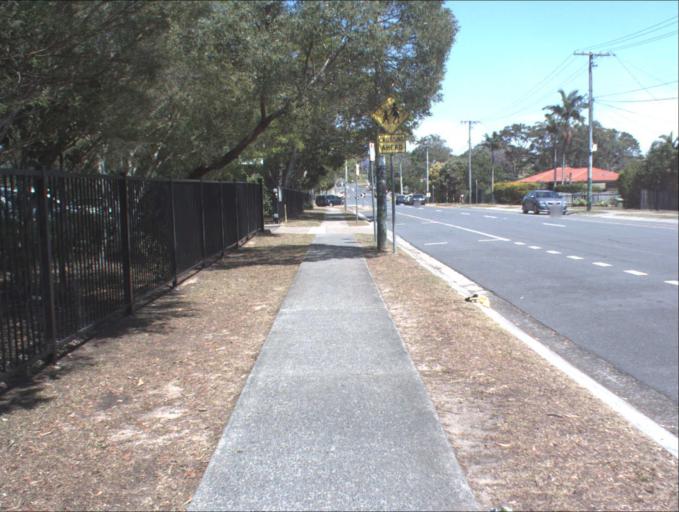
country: AU
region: Queensland
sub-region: Logan
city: Rochedale South
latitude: -27.5907
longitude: 153.1308
